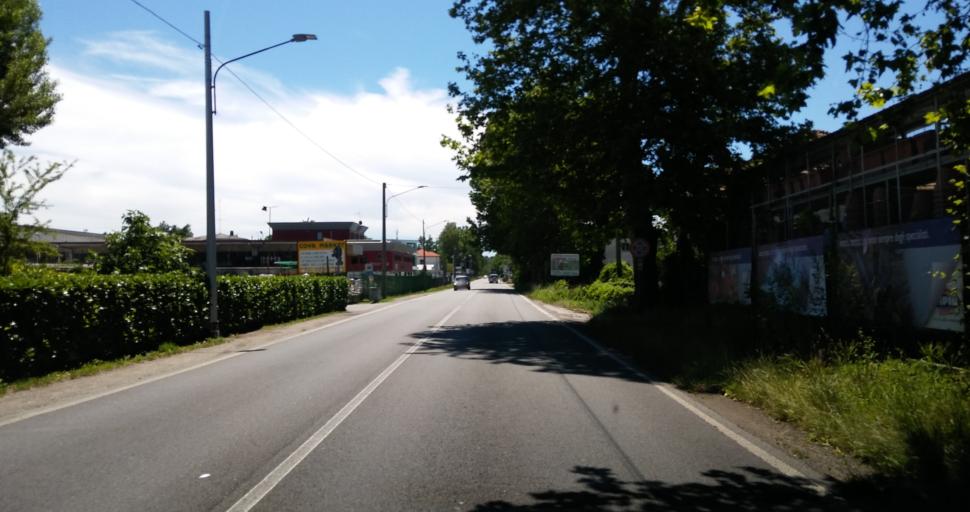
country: IT
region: Lombardy
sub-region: Provincia di Varese
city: Vergiate
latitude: 45.7158
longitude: 8.6923
